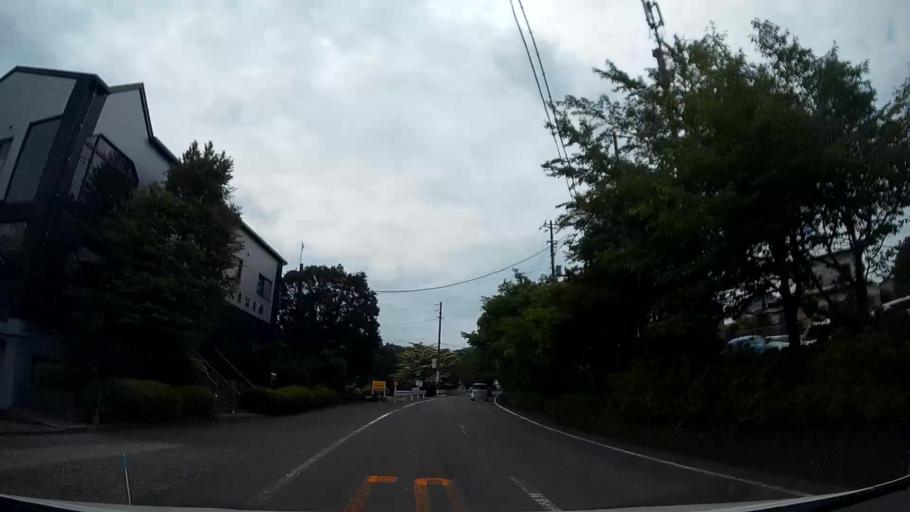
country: JP
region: Shizuoka
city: Ito
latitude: 34.9050
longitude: 139.1157
